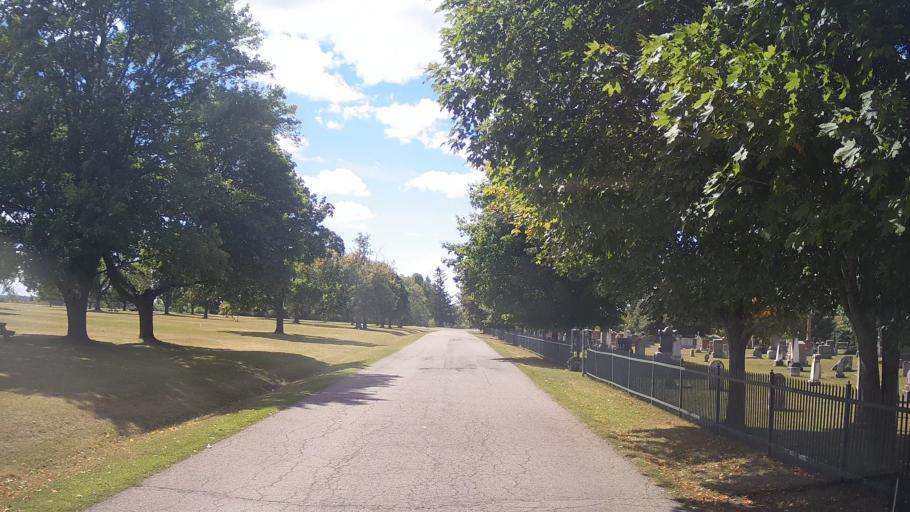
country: US
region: New York
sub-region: St. Lawrence County
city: Ogdensburg
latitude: 44.8317
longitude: -75.3147
